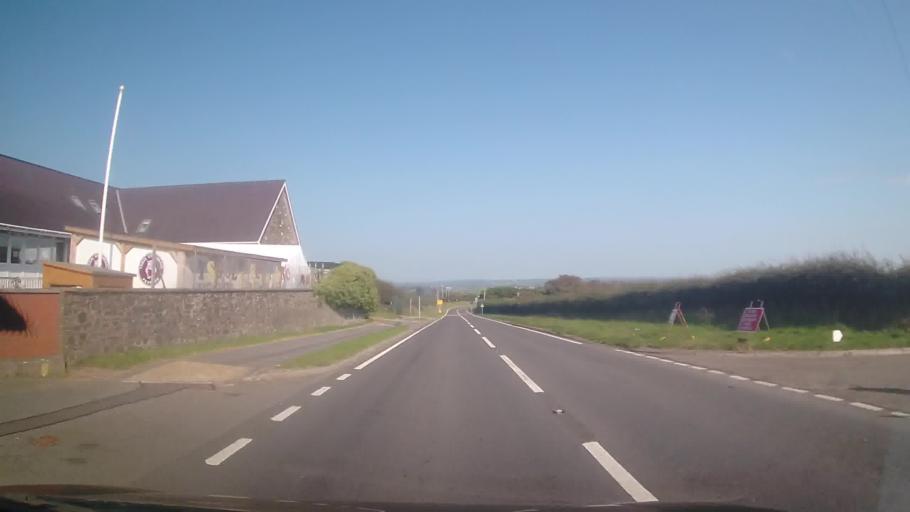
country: GB
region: Wales
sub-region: County of Ceredigion
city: Aberporth
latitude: 52.1056
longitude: -4.5946
